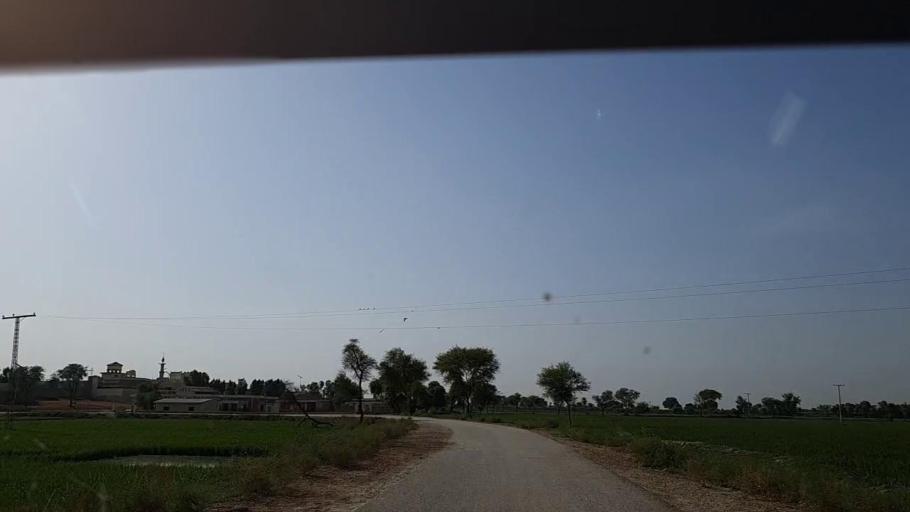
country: PK
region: Sindh
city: Phulji
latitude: 26.9905
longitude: 67.6534
